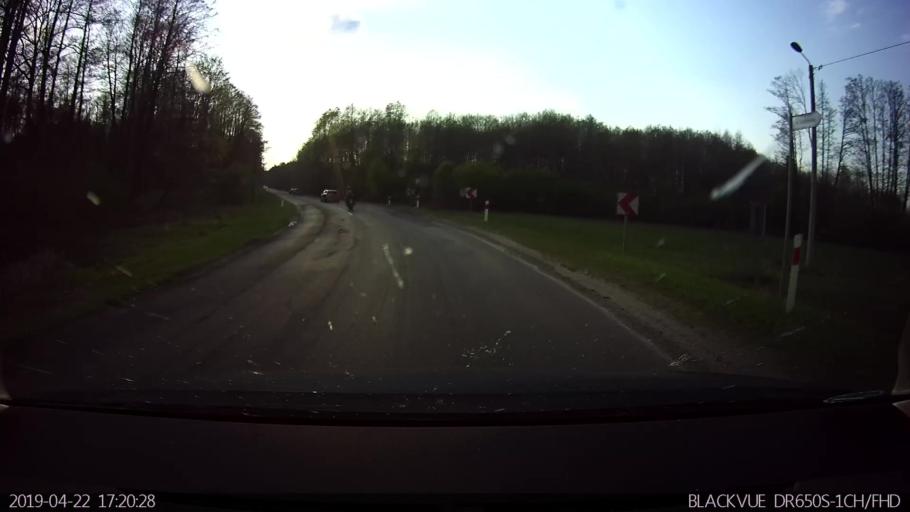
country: PL
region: Masovian Voivodeship
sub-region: Powiat sokolowski
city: Repki
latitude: 52.3888
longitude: 22.3817
